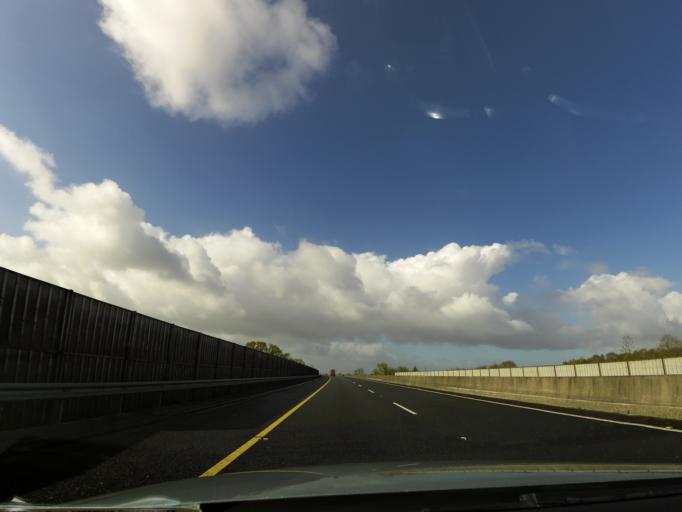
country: IE
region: Munster
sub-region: County Limerick
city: Castleconnell
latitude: 52.7108
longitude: -8.4796
